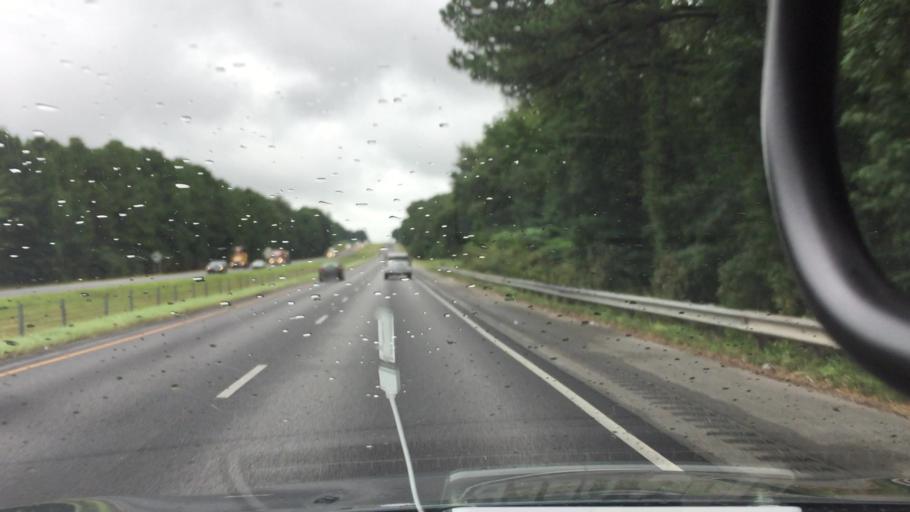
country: US
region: Alabama
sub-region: Lee County
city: Opelika
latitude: 32.6246
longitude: -85.3858
